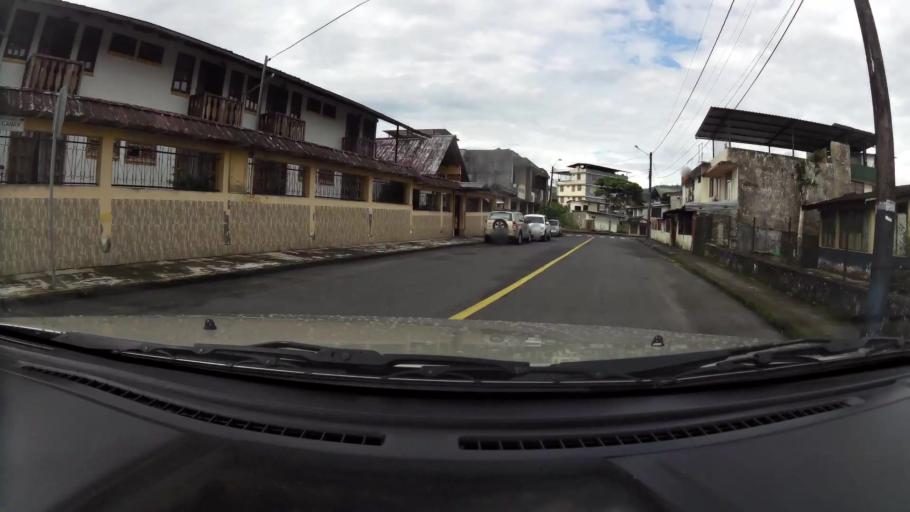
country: EC
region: Pastaza
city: Puyo
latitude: -1.4818
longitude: -77.9985
